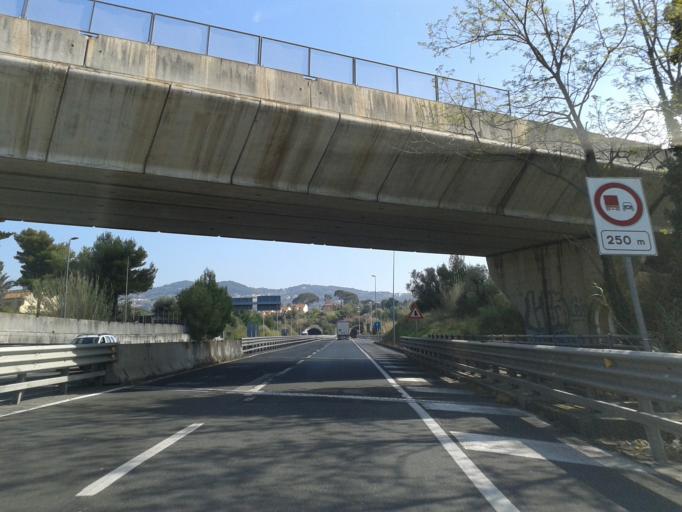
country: IT
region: Tuscany
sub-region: Provincia di Livorno
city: Livorno
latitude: 43.5123
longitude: 10.3335
